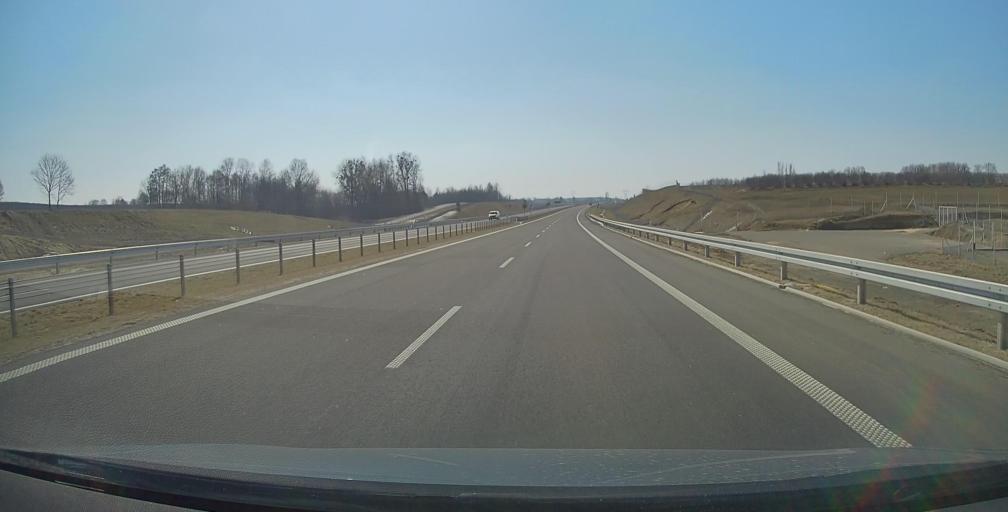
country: PL
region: Lublin Voivodeship
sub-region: Powiat krasnicki
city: Szastarka
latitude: 50.8152
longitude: 22.2999
